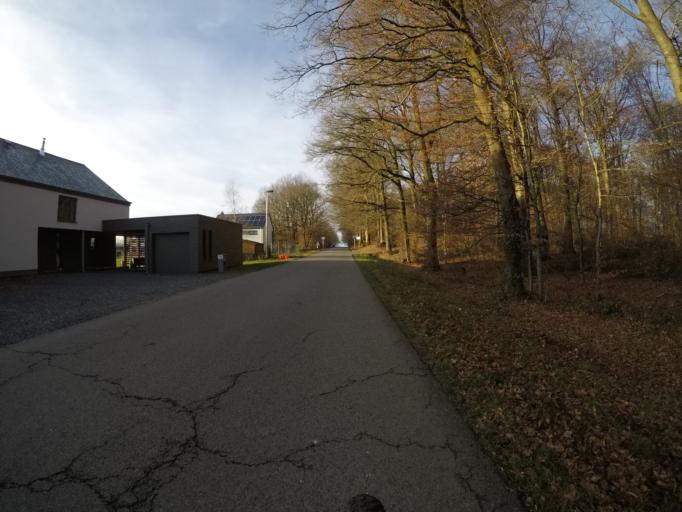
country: BE
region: Wallonia
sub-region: Province du Luxembourg
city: Tintigny
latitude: 49.6786
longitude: 5.4801
